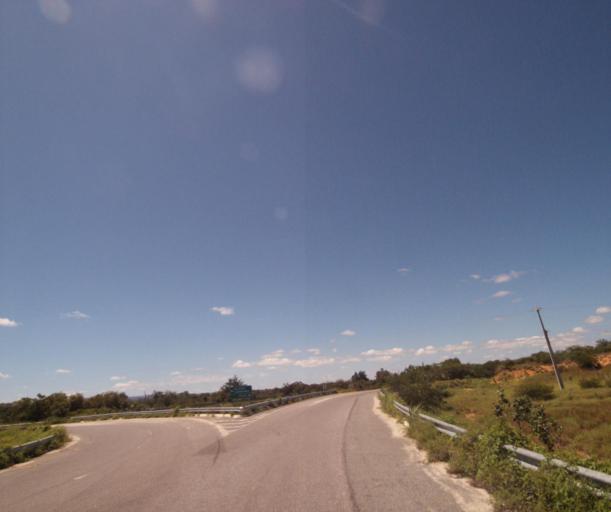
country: BR
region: Bahia
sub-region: Carinhanha
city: Carinhanha
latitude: -14.3197
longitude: -43.7800
